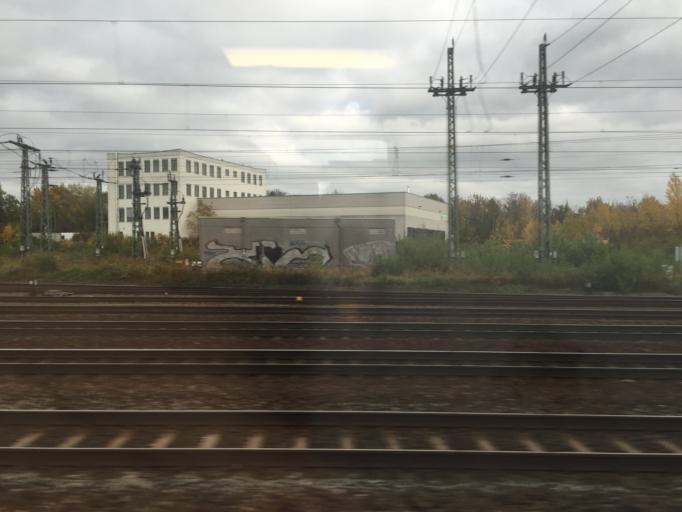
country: DE
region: Saxony
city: Leipzig
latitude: 51.3791
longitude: 12.3961
